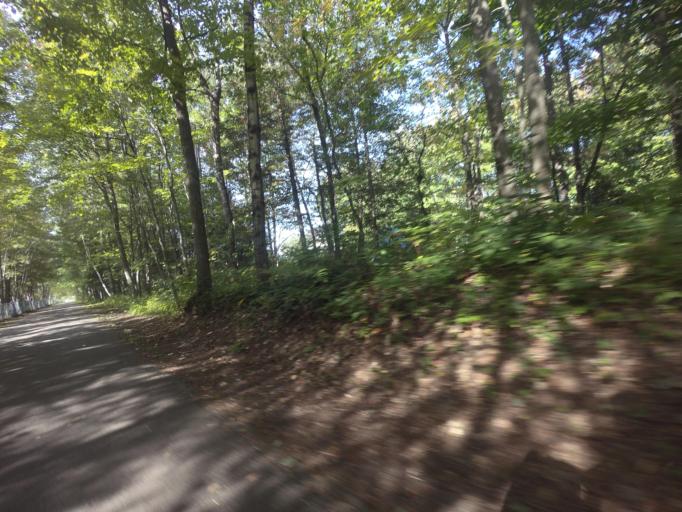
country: CA
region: Quebec
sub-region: Laurentides
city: Blainville
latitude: 45.7056
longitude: -73.9101
